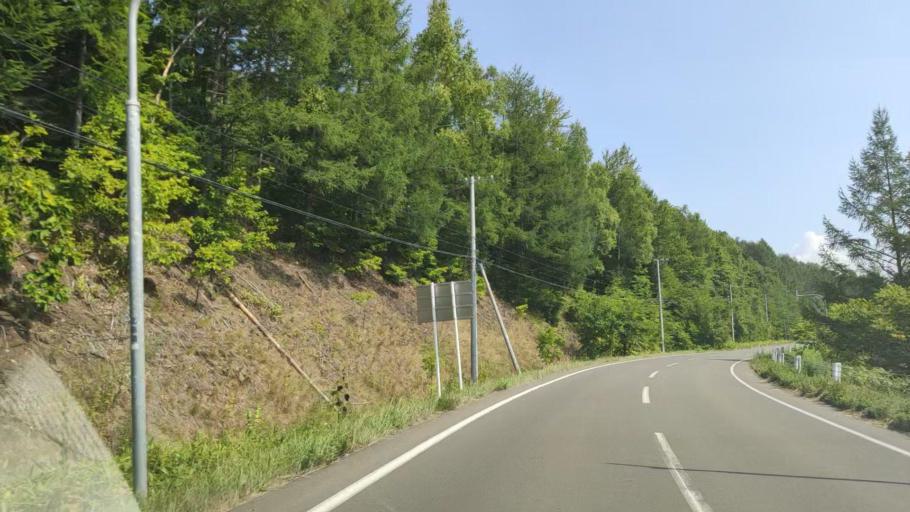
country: JP
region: Hokkaido
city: Shimo-furano
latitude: 43.4259
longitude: 142.4002
